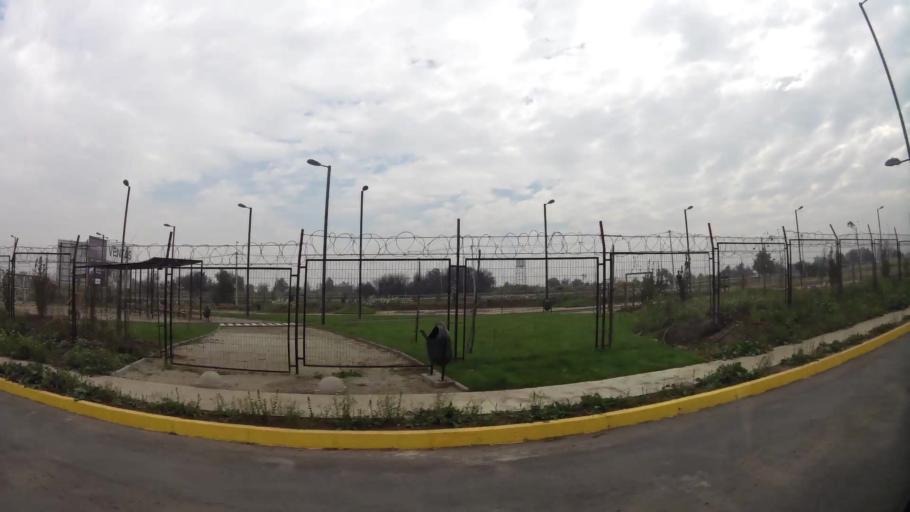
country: CL
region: Santiago Metropolitan
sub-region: Provincia de Chacabuco
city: Chicureo Abajo
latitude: -33.2209
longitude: -70.6770
